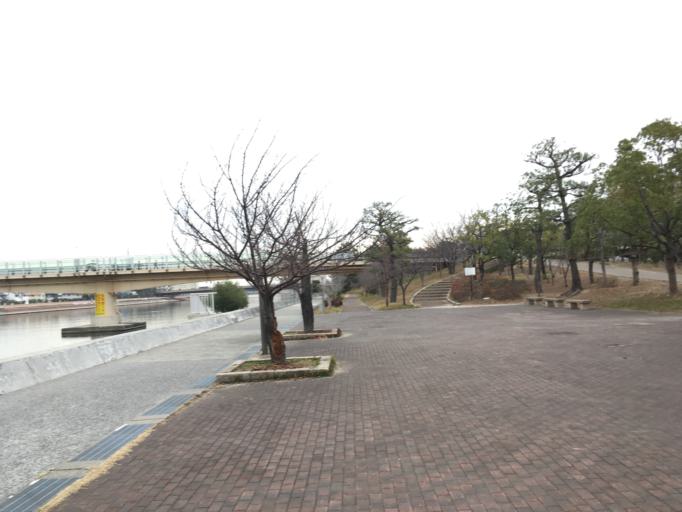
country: JP
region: Hyogo
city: Nishinomiya-hama
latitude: 34.7149
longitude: 135.3155
